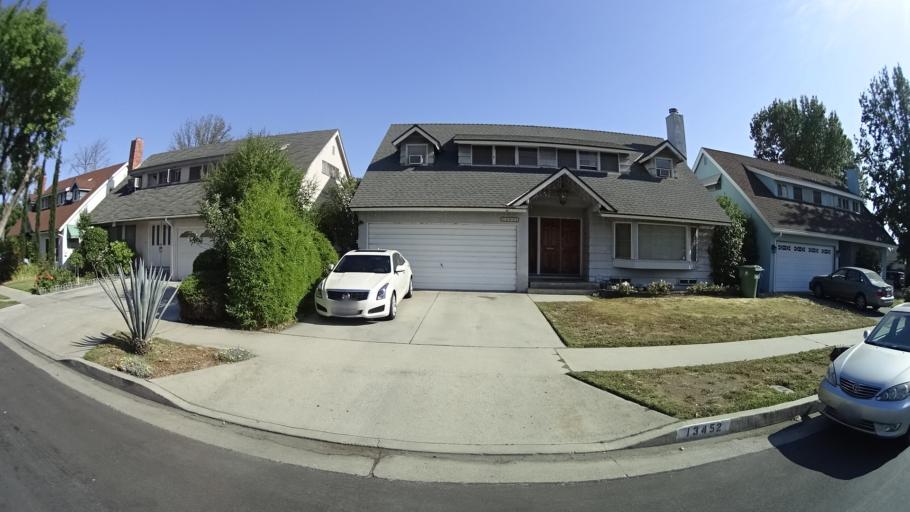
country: US
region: California
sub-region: Los Angeles County
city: Van Nuys
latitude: 34.2189
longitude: -118.4264
